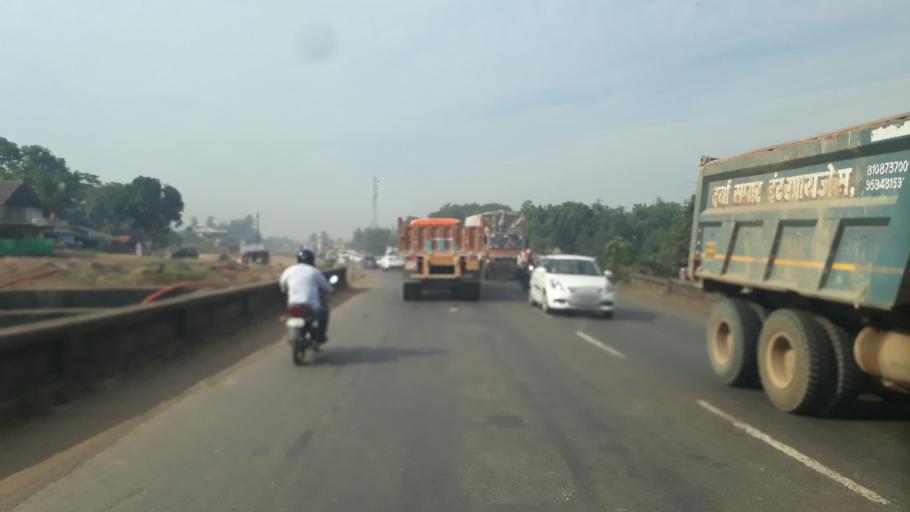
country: IN
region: Maharashtra
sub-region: Raigarh
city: Pen
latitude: 18.7260
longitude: 73.0737
